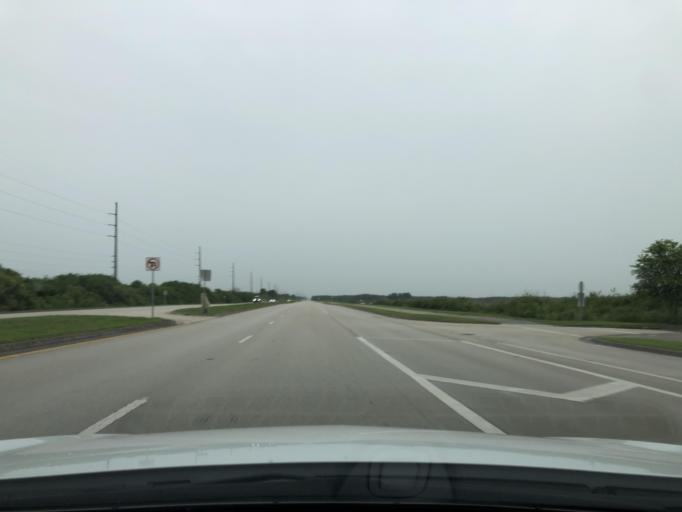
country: US
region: Florida
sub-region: Collier County
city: Immokalee
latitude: 26.2945
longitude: -81.4467
